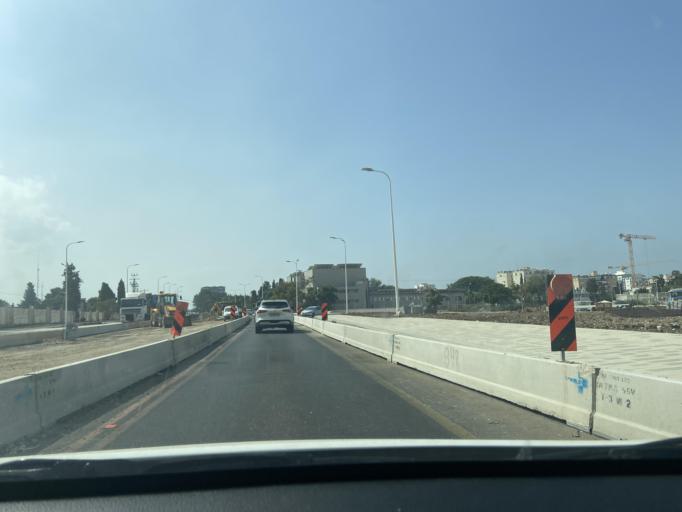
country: IL
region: Northern District
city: Nahariya
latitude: 33.0117
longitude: 35.1013
